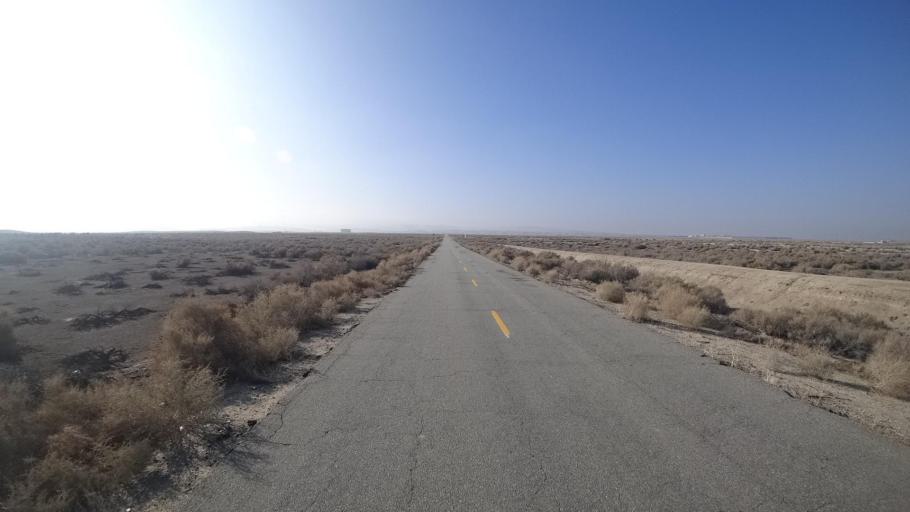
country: US
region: California
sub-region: Kern County
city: Maricopa
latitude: 35.1011
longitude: -119.3793
